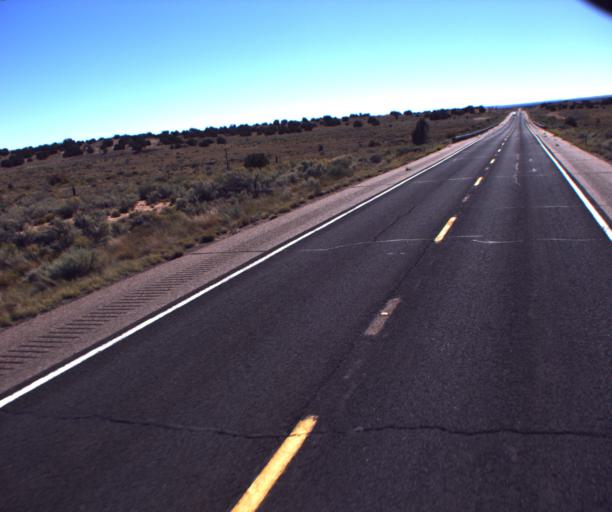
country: US
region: Arizona
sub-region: Navajo County
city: Snowflake
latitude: 34.6797
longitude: -109.7334
